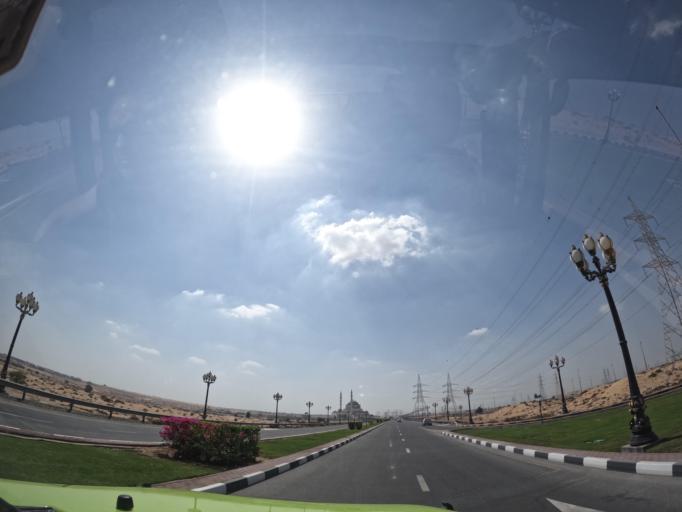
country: AE
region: Ash Shariqah
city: Sharjah
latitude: 25.2478
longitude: 55.5726
